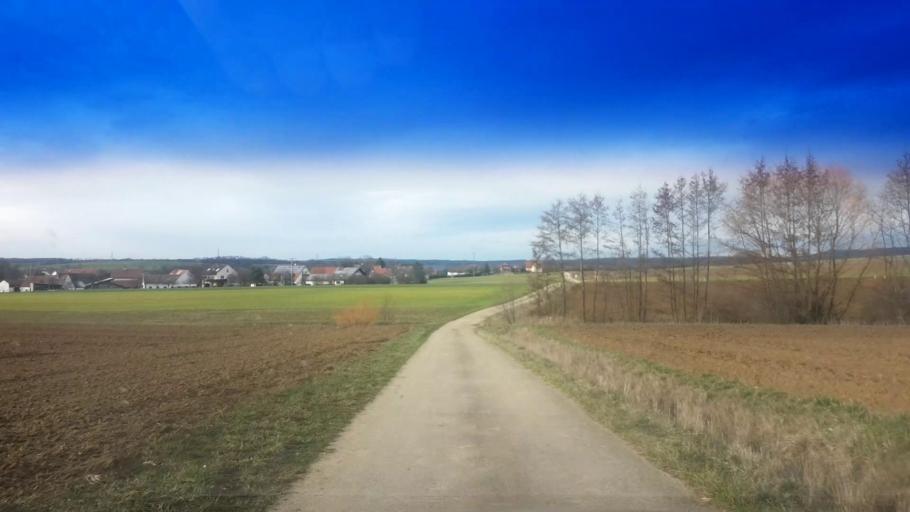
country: DE
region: Bavaria
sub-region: Upper Franconia
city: Litzendorf
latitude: 49.9298
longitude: 10.9887
